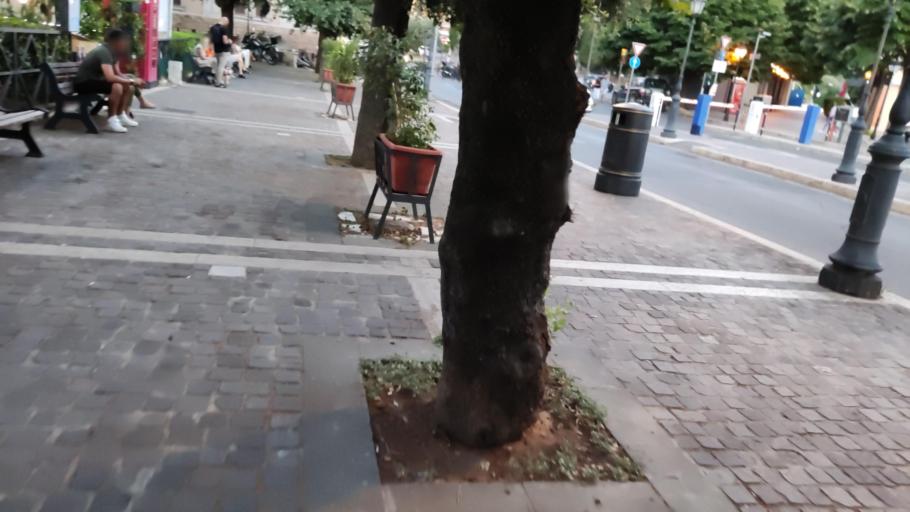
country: IT
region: Latium
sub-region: Citta metropolitana di Roma Capitale
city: Tivoli
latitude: 41.9655
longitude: 12.8005
